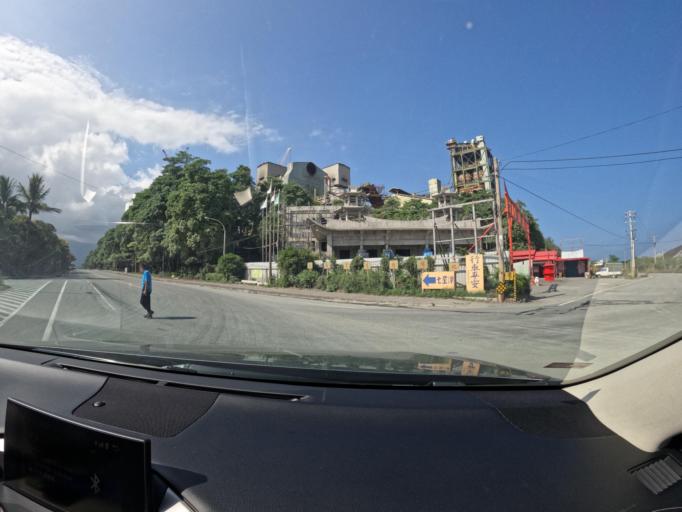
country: TW
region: Taiwan
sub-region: Hualien
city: Hualian
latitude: 24.0080
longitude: 121.6372
